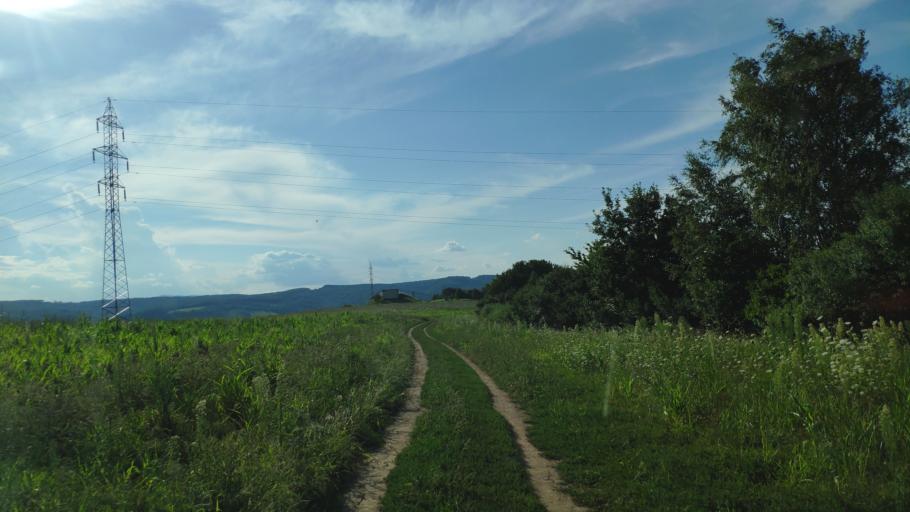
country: SK
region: Presovsky
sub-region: Okres Presov
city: Presov
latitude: 48.9140
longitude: 21.2708
